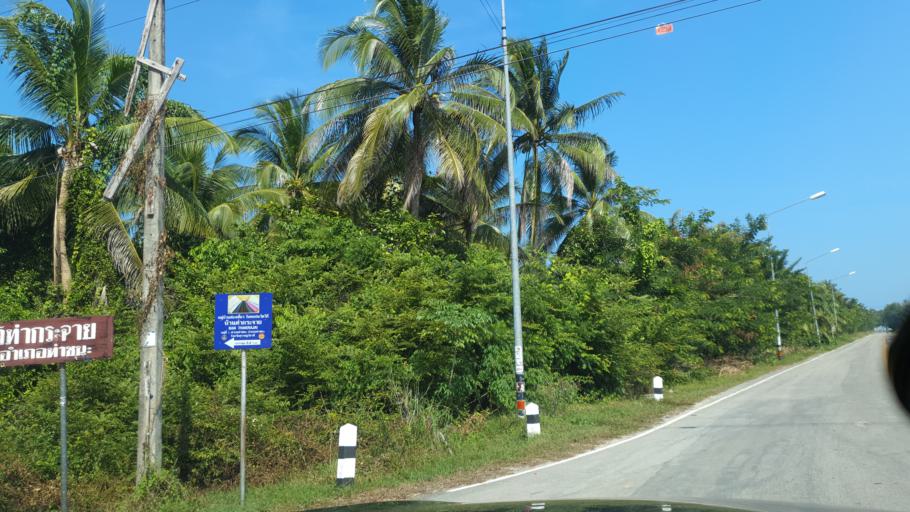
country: TH
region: Surat Thani
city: Tha Chana
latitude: 9.5871
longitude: 99.2019
